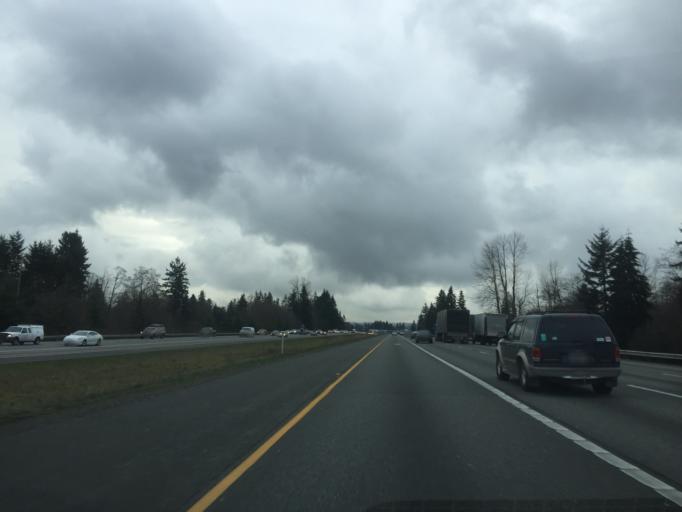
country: US
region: Washington
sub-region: Snohomish County
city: Martha Lake
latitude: 47.8611
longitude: -122.2491
